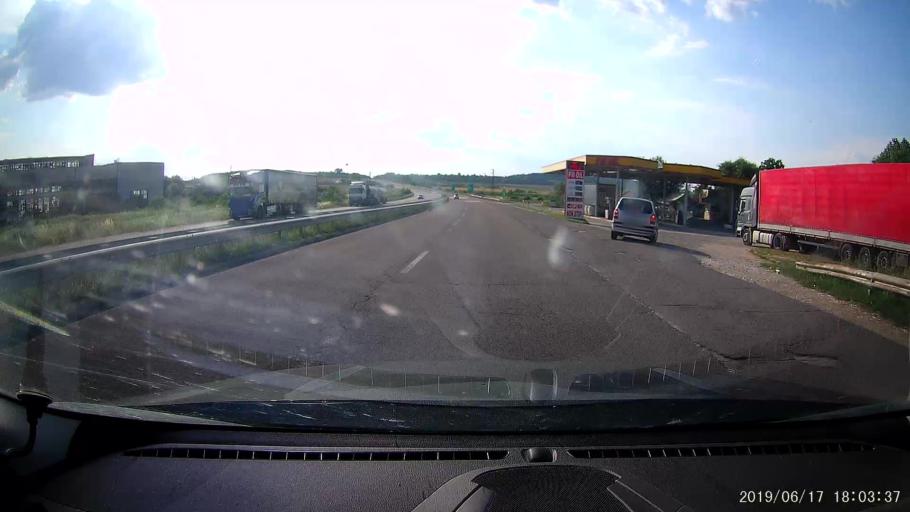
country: BG
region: Khaskovo
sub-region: Obshtina Svilengrad
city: Svilengrad
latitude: 41.7797
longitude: 26.2159
